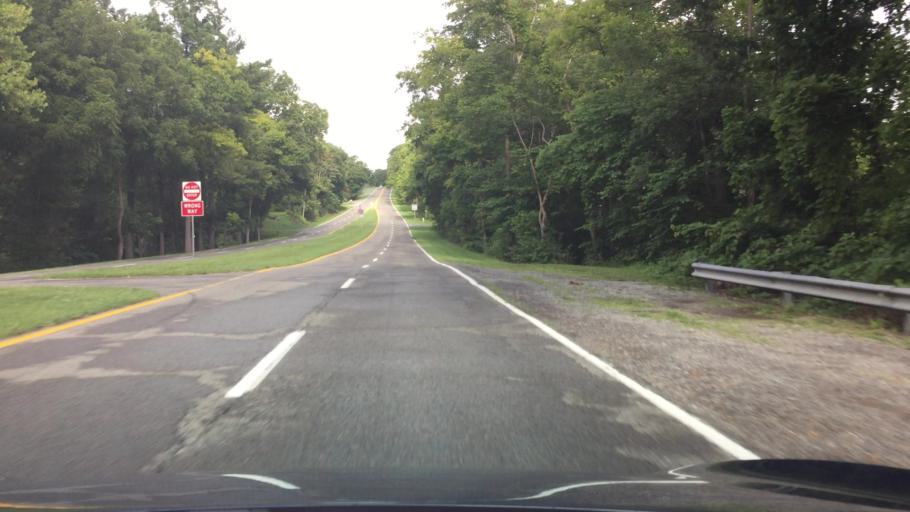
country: US
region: Virginia
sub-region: Pulaski County
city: Pulaski
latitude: 36.9497
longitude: -80.9021
